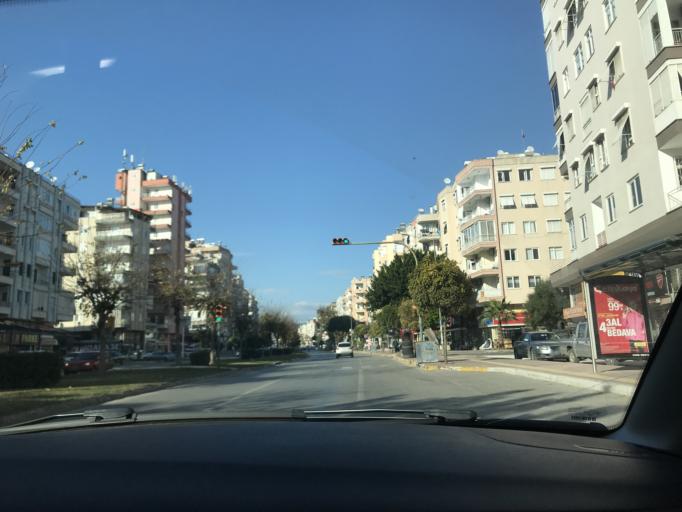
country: TR
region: Antalya
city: Antalya
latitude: 36.9035
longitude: 30.7010
